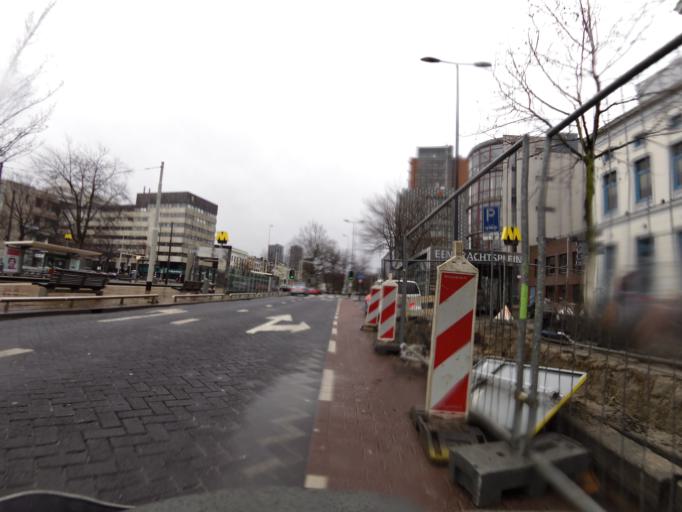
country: NL
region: South Holland
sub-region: Gemeente Rotterdam
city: Rotterdam
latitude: 51.9168
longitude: 4.4729
